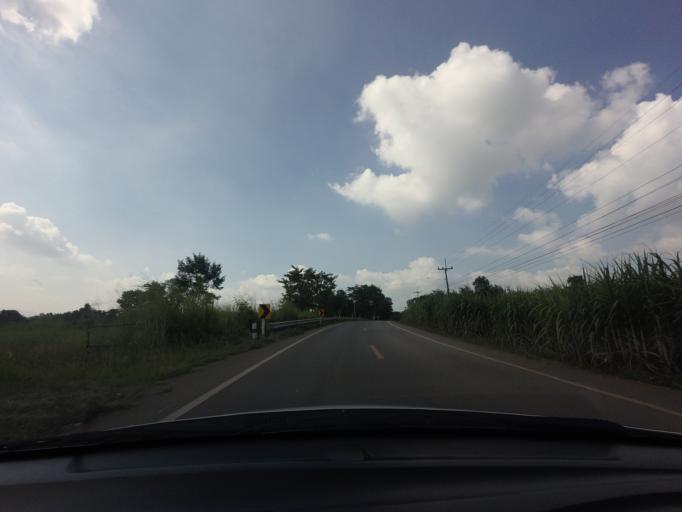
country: TH
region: Nakhon Ratchasima
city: Wang Nam Khiao
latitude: 14.4541
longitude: 101.6661
